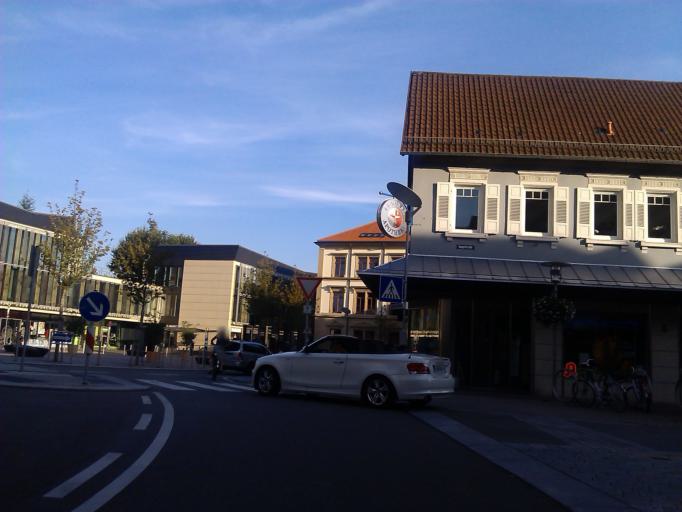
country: DE
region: Baden-Wuerttemberg
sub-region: Karlsruhe Region
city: Walldorf
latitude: 49.3033
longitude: 8.6426
